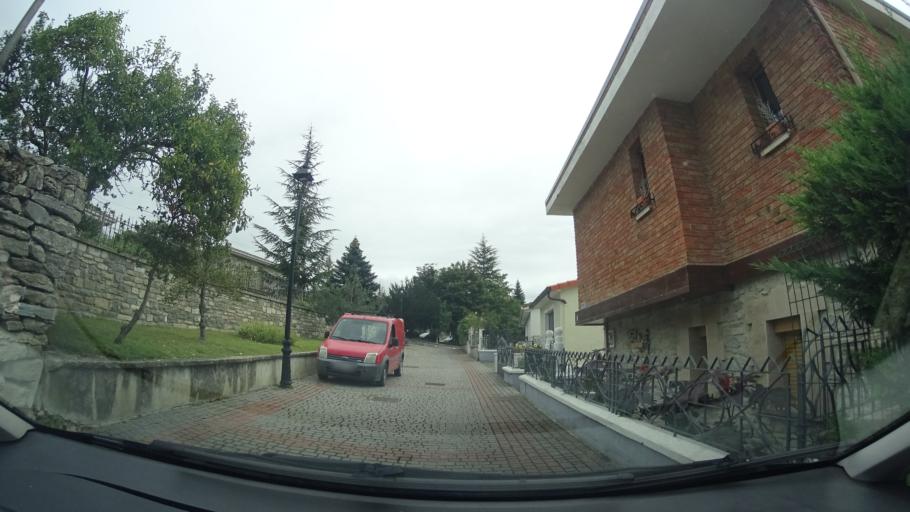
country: ES
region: Basque Country
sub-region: Provincia de Alava
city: Arminon
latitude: 42.8183
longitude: -2.8095
